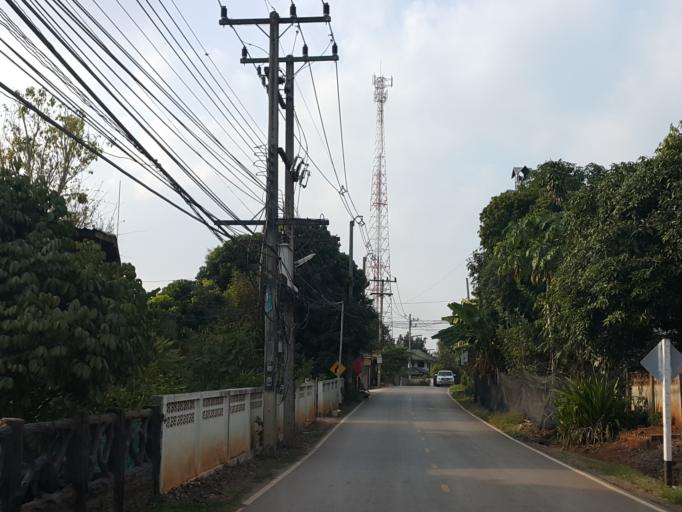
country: TH
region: Chiang Mai
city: Mae On
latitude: 18.9098
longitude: 99.2383
